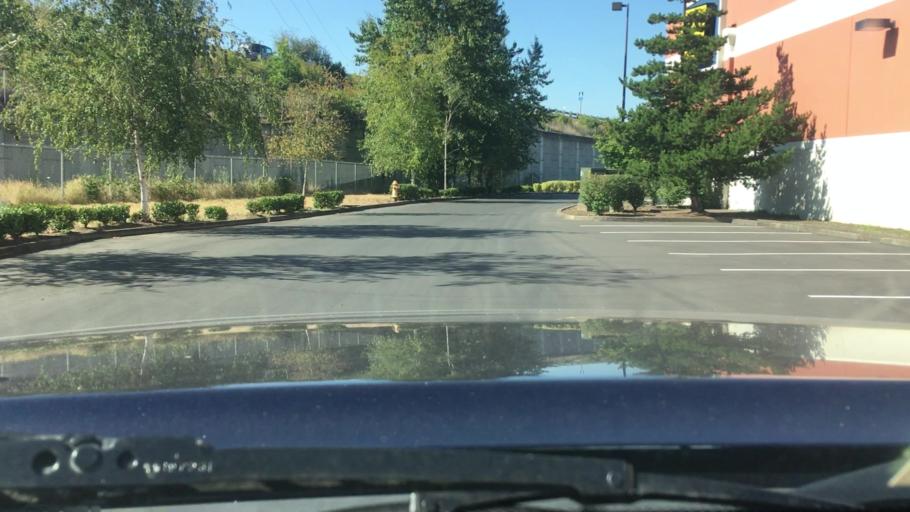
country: US
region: Oregon
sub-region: Lane County
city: Springfield
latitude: 44.0814
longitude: -123.0458
